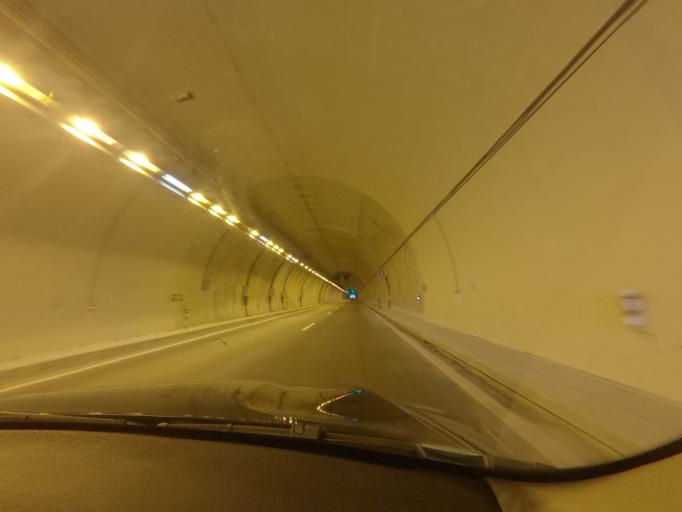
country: PT
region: Viseu
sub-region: Castro Daire
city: Castro Daire
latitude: 40.8980
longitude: -7.9146
